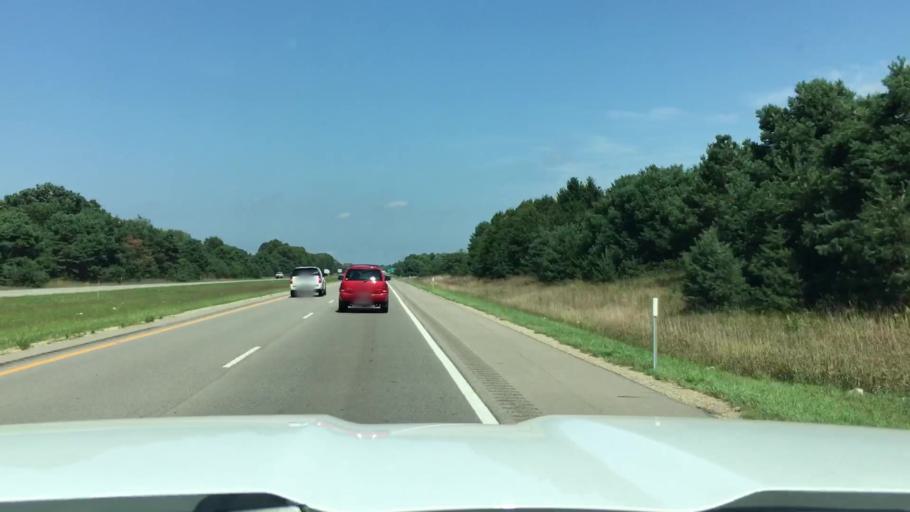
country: US
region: Michigan
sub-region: Kalamazoo County
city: Portage
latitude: 42.2104
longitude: -85.6430
